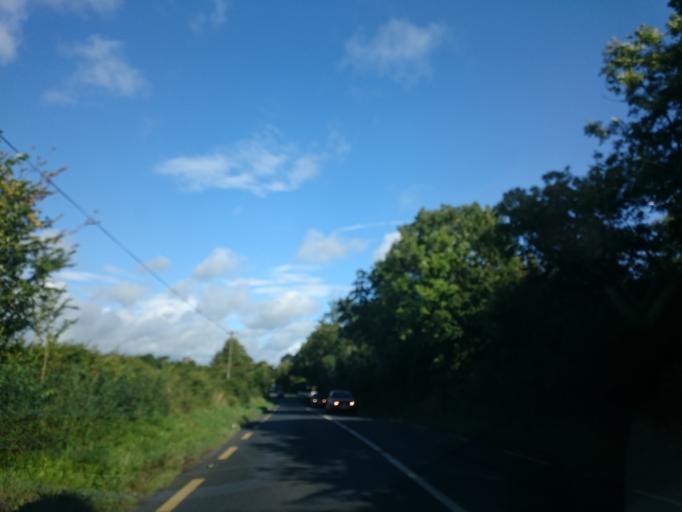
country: IE
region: Leinster
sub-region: Kilkenny
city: Kilkenny
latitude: 52.6877
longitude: -7.2565
